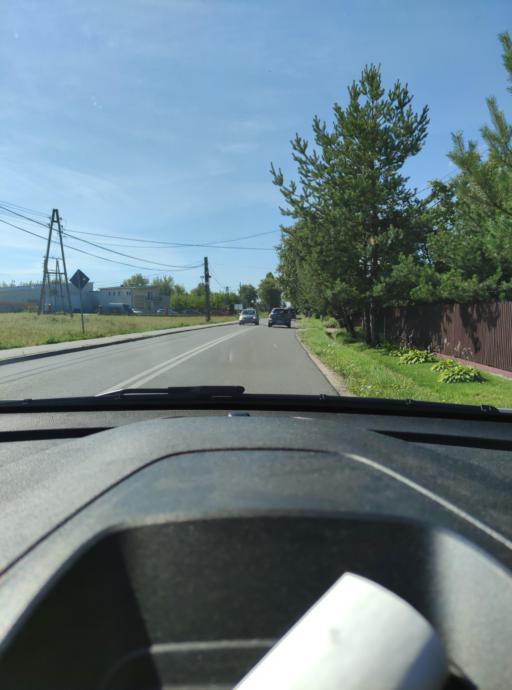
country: PL
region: Masovian Voivodeship
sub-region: Powiat pruszkowski
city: Rybie
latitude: 52.1298
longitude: 20.9284
